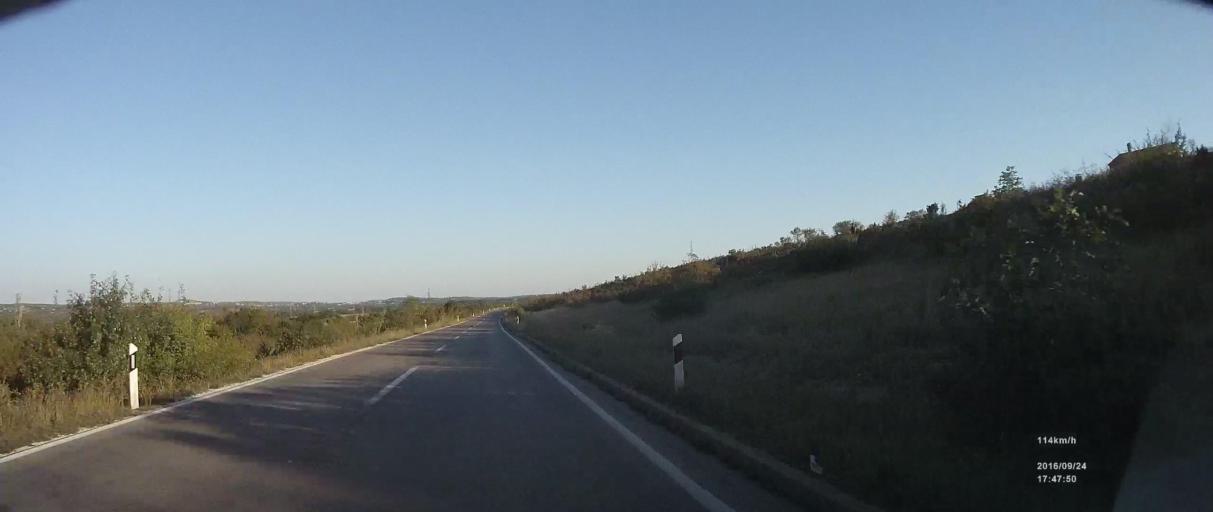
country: HR
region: Zadarska
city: Polaca
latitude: 44.0704
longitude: 15.5292
